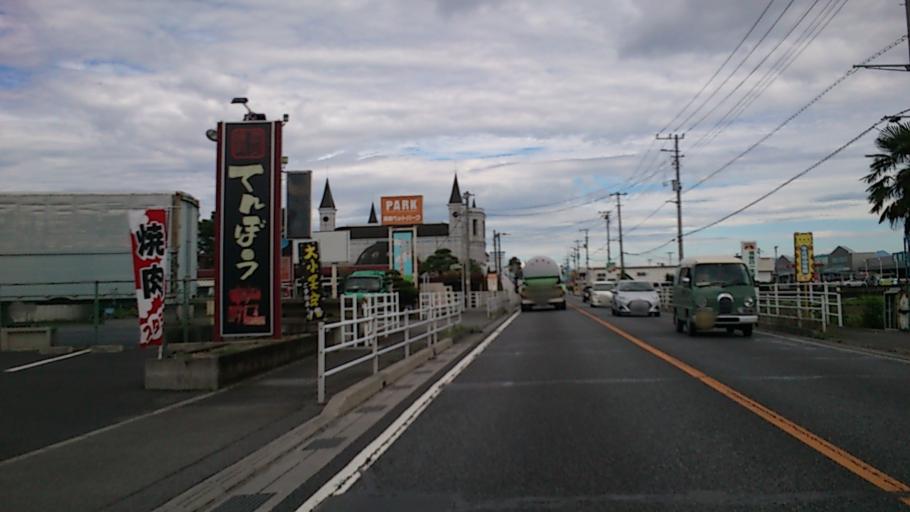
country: JP
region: Saitama
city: Honjo
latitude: 36.2549
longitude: 139.1615
